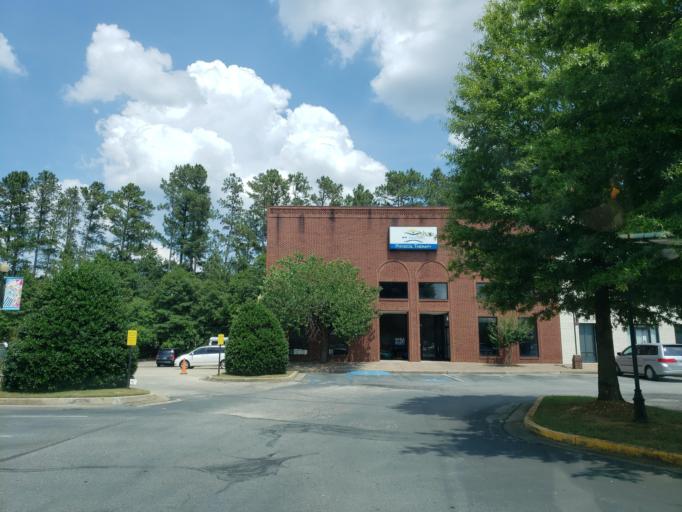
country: US
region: Georgia
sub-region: Bartow County
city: Cartersville
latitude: 34.1533
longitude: -84.8165
